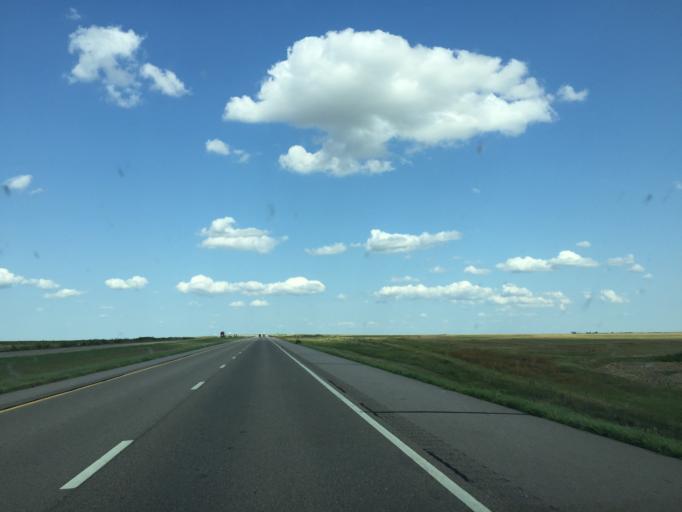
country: US
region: Kansas
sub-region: Trego County
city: WaKeeney
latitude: 39.0230
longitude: -100.0335
